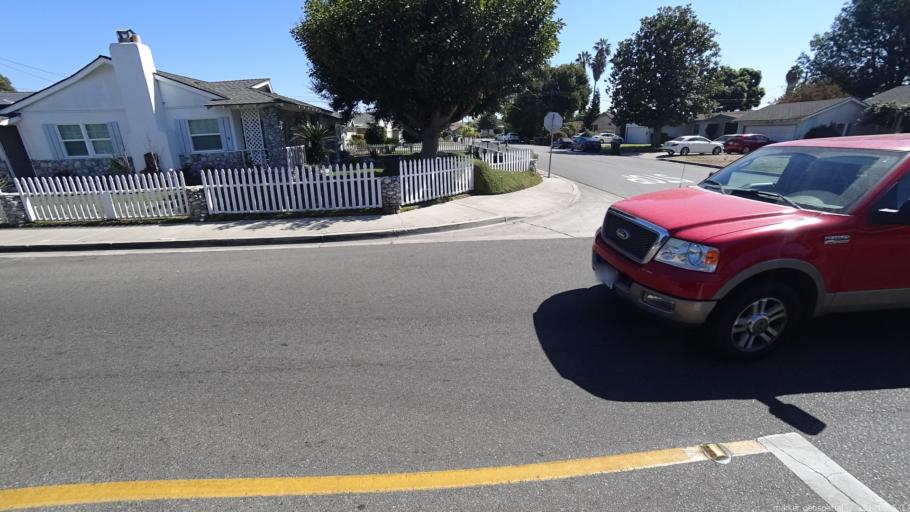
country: US
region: California
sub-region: Orange County
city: Garden Grove
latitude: 33.7700
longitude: -117.9676
